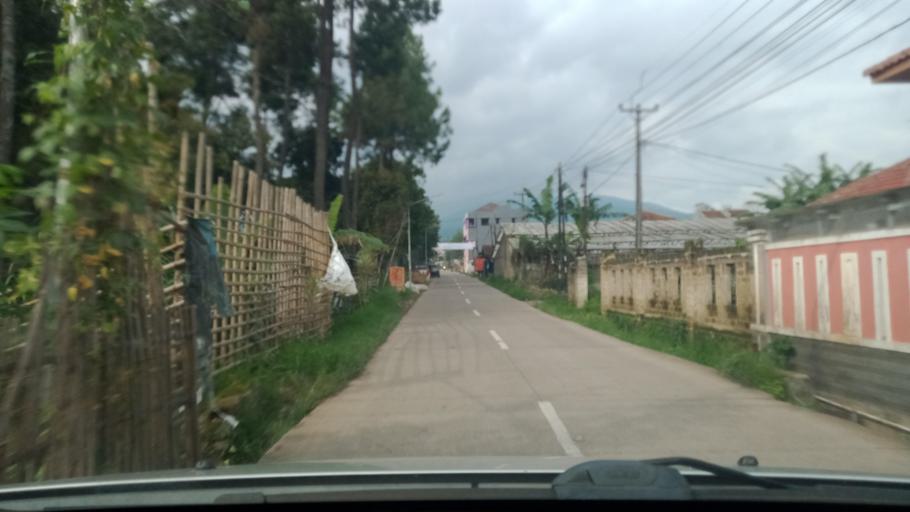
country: ID
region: West Java
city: Lembang
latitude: -6.8157
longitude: 107.5758
